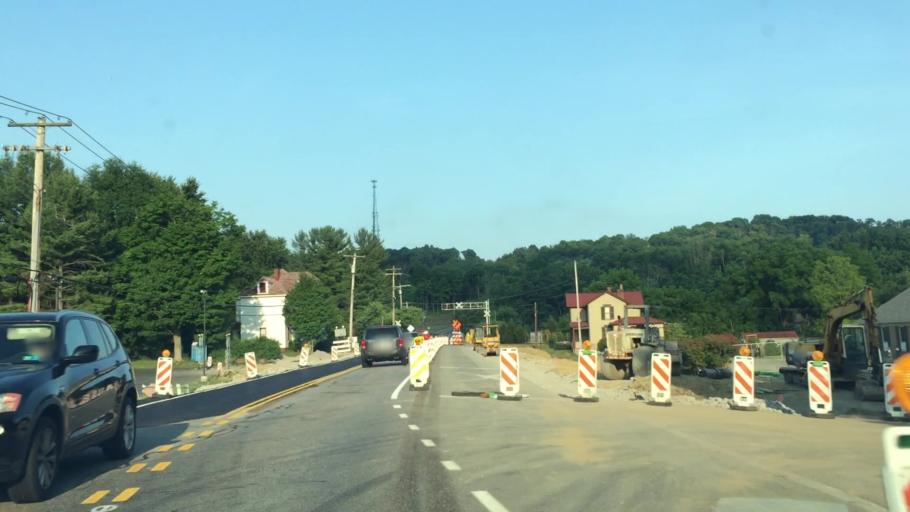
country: US
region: Pennsylvania
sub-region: Washington County
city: Thompsonville
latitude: 40.3187
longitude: -80.1149
